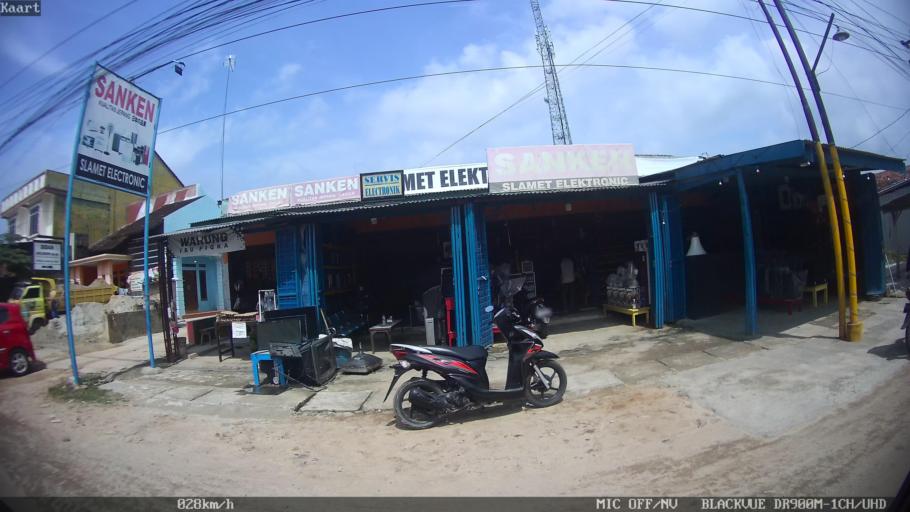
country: ID
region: Lampung
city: Kedaton
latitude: -5.3361
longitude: 105.2930
